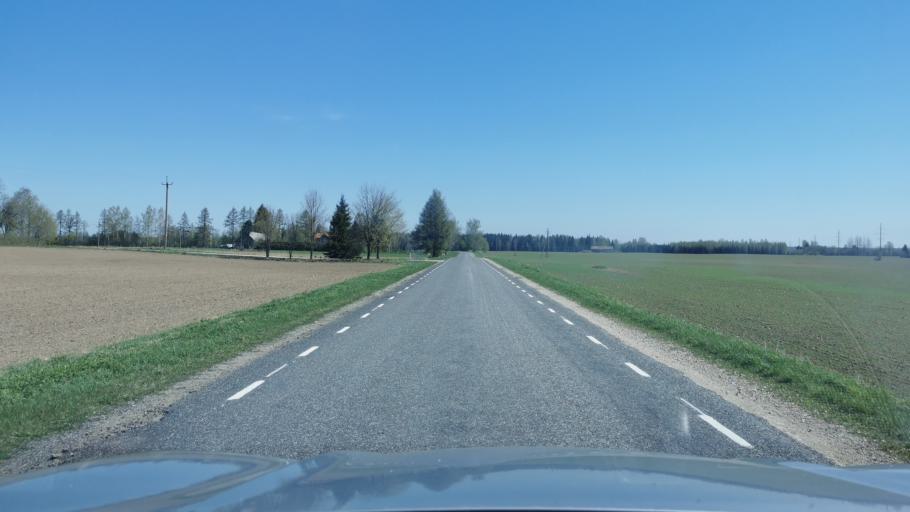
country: EE
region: Laeaene-Virumaa
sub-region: Vinni vald
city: Vinni
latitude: 59.0734
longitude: 26.5738
